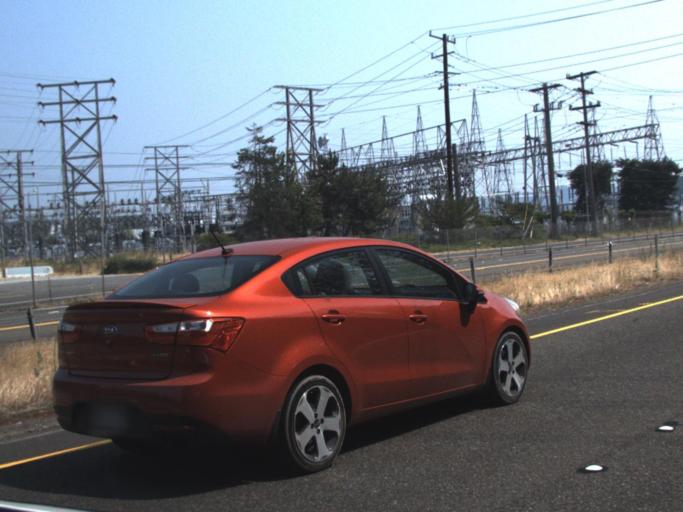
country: US
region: Washington
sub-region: King County
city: Boulevard Park
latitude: 47.5144
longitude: -122.3096
